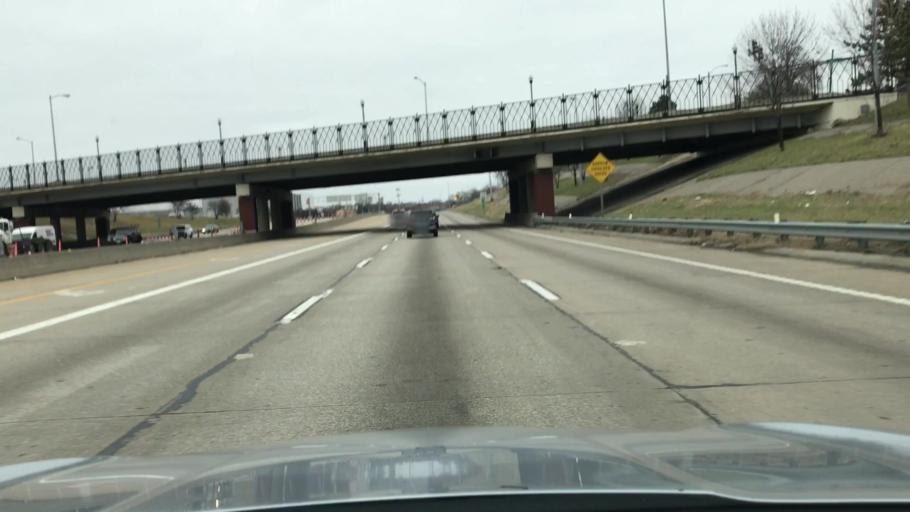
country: US
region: Missouri
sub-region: Saint Louis County
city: Pine Lawn
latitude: 38.6883
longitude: -90.2501
